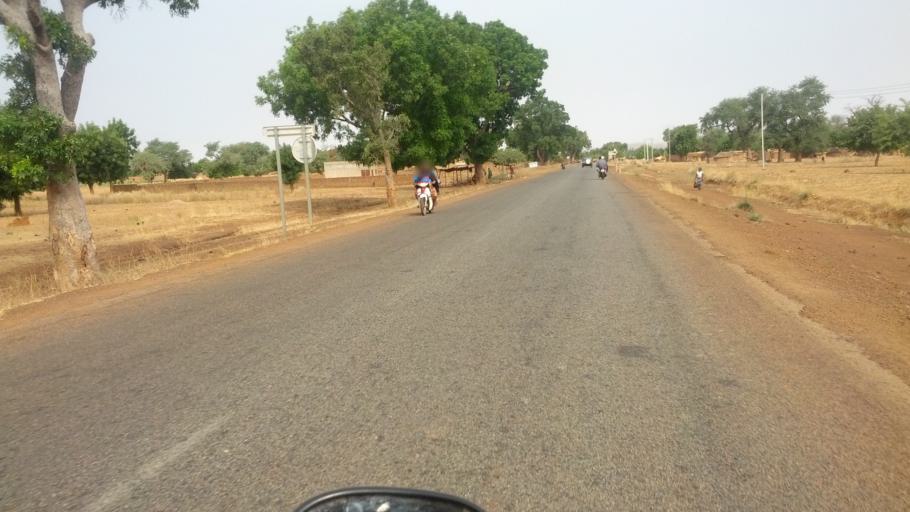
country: BF
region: Centre-Nord
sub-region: Province du Sanmatenga
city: Kaya
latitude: 12.8981
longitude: -1.0773
